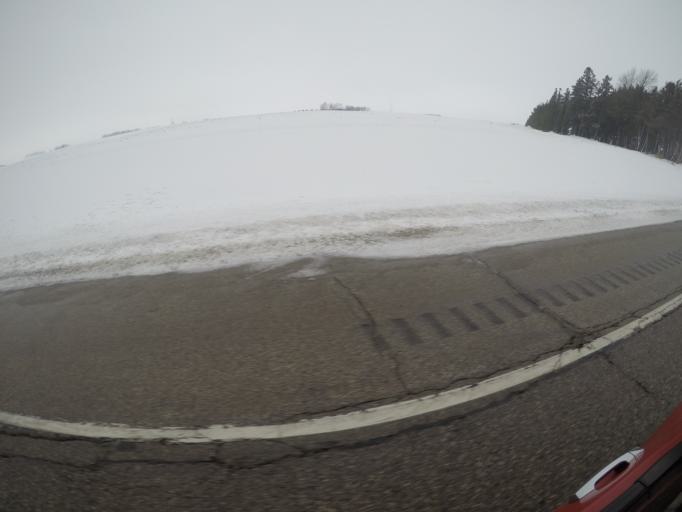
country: US
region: Minnesota
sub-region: Goodhue County
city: Wanamingo
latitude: 44.3727
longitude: -92.8070
